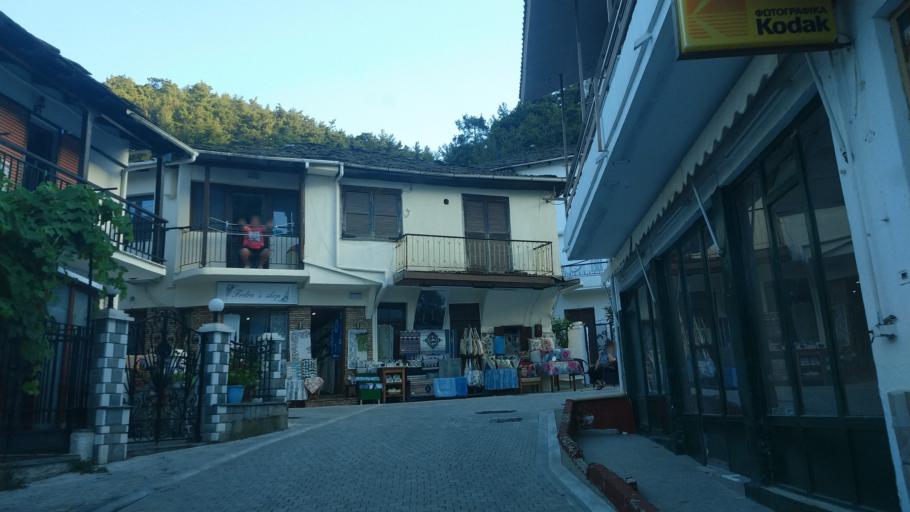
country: GR
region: East Macedonia and Thrace
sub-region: Nomos Kavalas
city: Potamia
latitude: 40.7305
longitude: 24.7277
